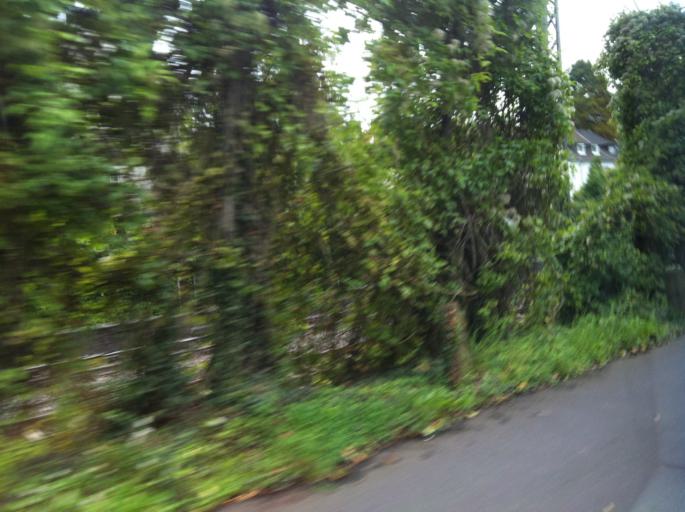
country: DE
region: North Rhine-Westphalia
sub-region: Regierungsbezirk Koln
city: Bonn
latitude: 50.7225
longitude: 7.1102
